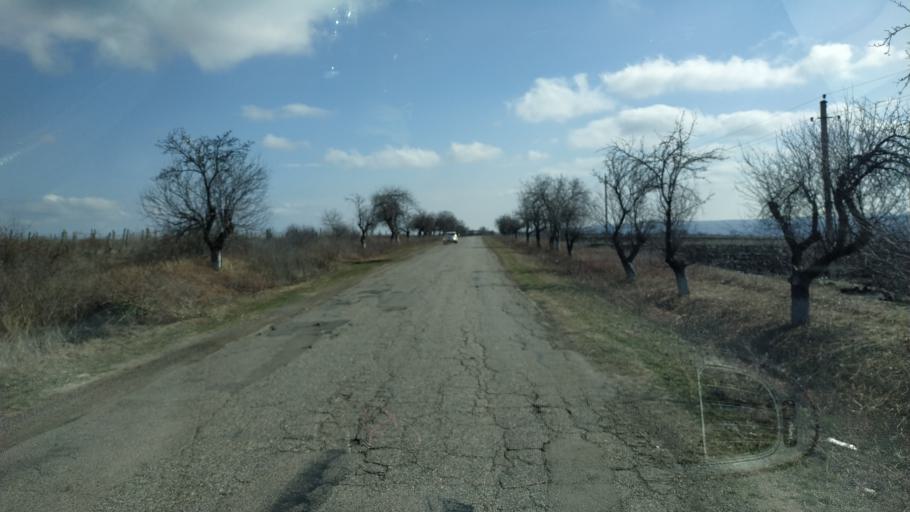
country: MD
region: Hincesti
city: Hincesti
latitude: 46.8512
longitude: 28.6476
